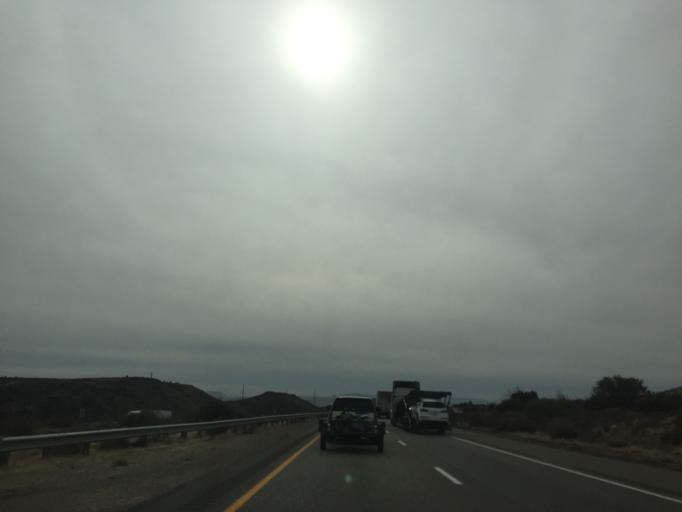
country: US
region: Utah
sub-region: Washington County
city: Toquerville
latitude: 37.2922
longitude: -113.3010
